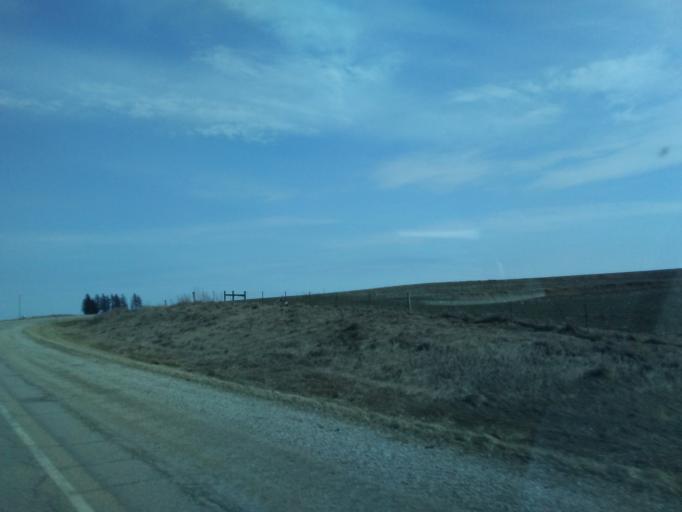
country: US
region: Iowa
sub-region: Allamakee County
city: Waukon
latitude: 43.2003
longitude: -91.3932
